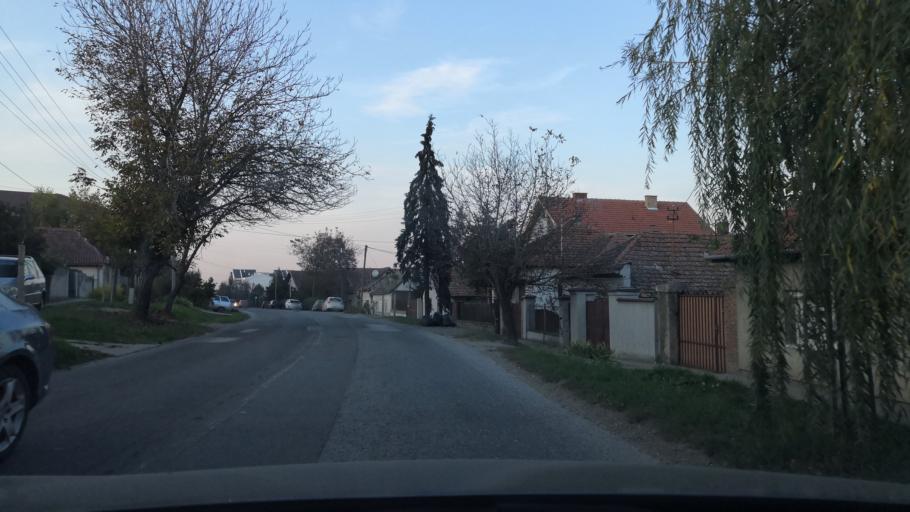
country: RS
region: Autonomna Pokrajina Vojvodina
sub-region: Juznobacki Okrug
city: Petrovaradin
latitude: 45.2358
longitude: 19.8850
